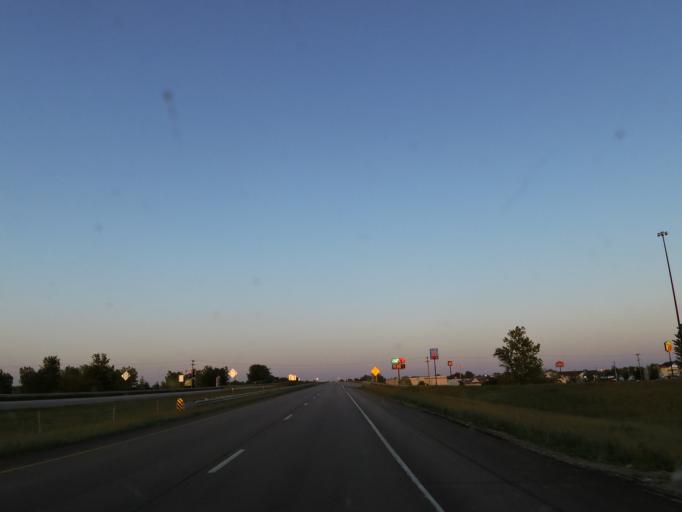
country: US
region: Indiana
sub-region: Montgomery County
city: Crawfordsville
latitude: 40.0800
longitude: -86.9066
